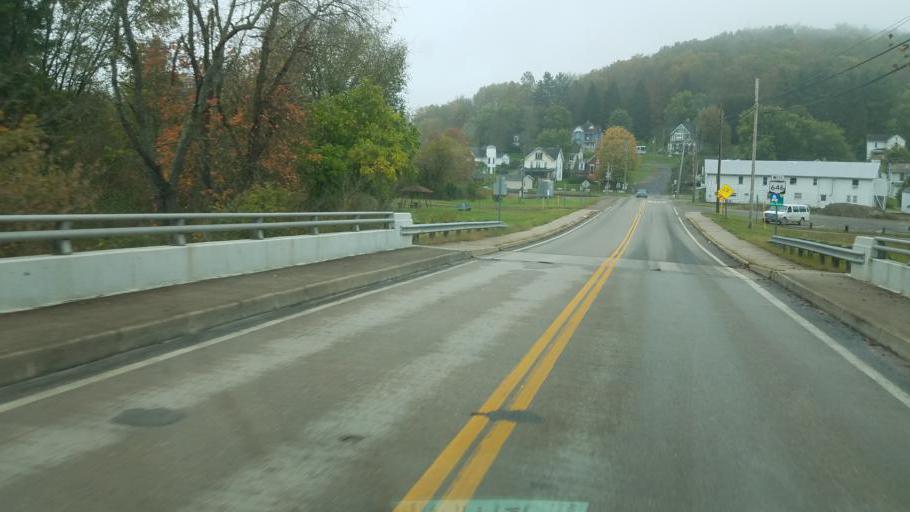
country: US
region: Ohio
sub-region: Harrison County
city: Cadiz
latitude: 40.3944
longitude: -81.0843
